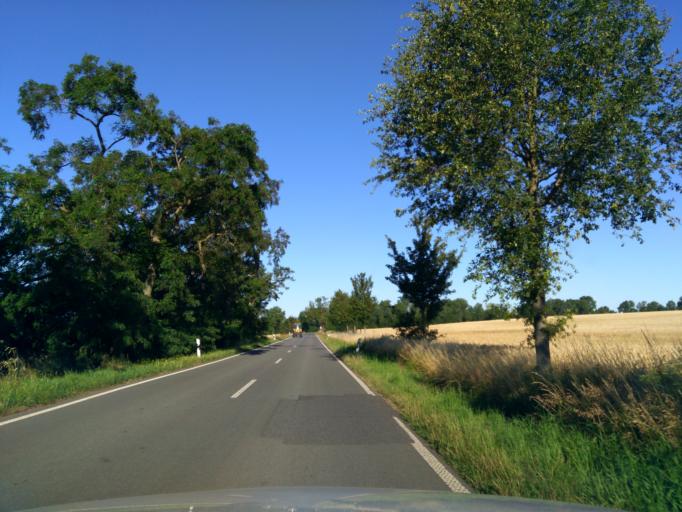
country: DE
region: Brandenburg
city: Fehrbellin
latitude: 52.7563
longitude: 12.7996
